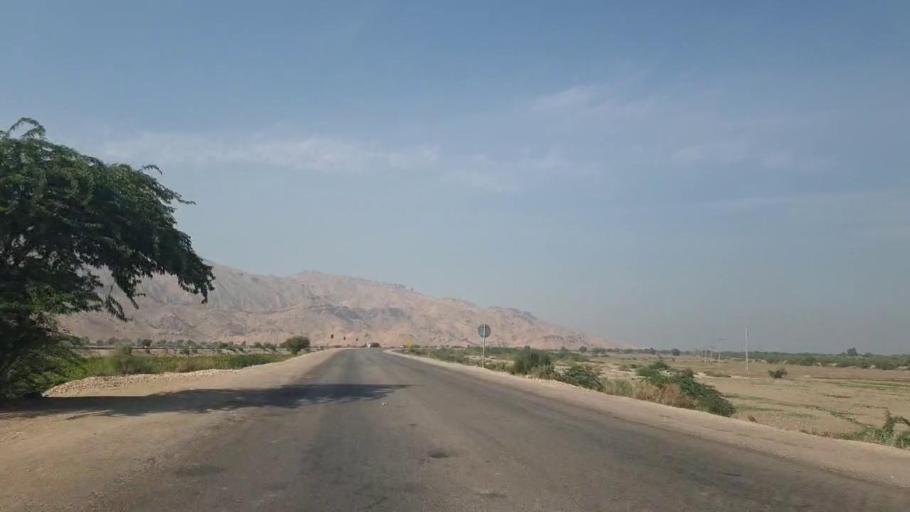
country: PK
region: Sindh
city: Sehwan
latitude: 26.2738
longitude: 67.9002
